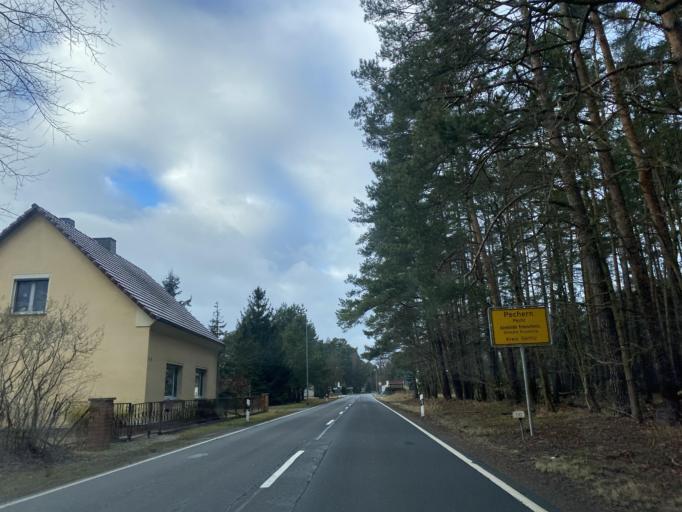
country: PL
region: Lubusz
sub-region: Powiat zarski
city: Przewoz
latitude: 51.4799
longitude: 14.8627
